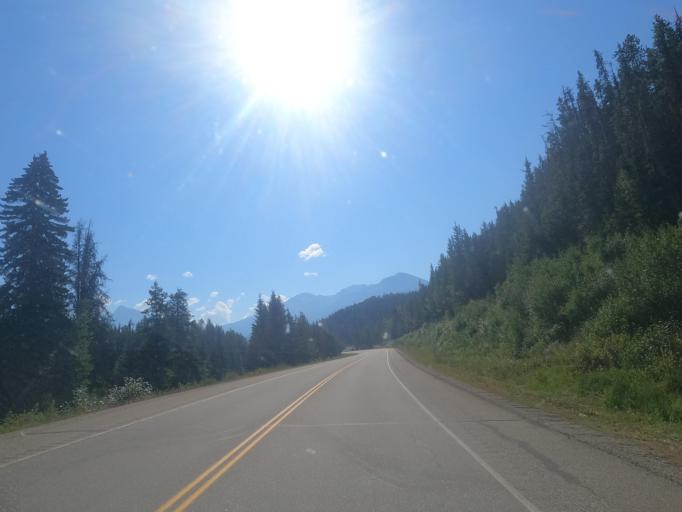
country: CA
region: Alberta
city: Jasper Park Lodge
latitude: 52.8612
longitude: -118.6413
